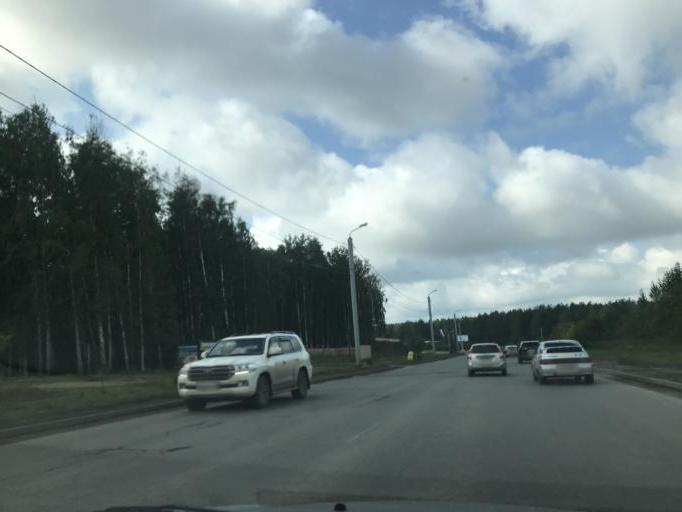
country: RU
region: Chelyabinsk
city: Roshchino
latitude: 55.2015
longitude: 61.2834
